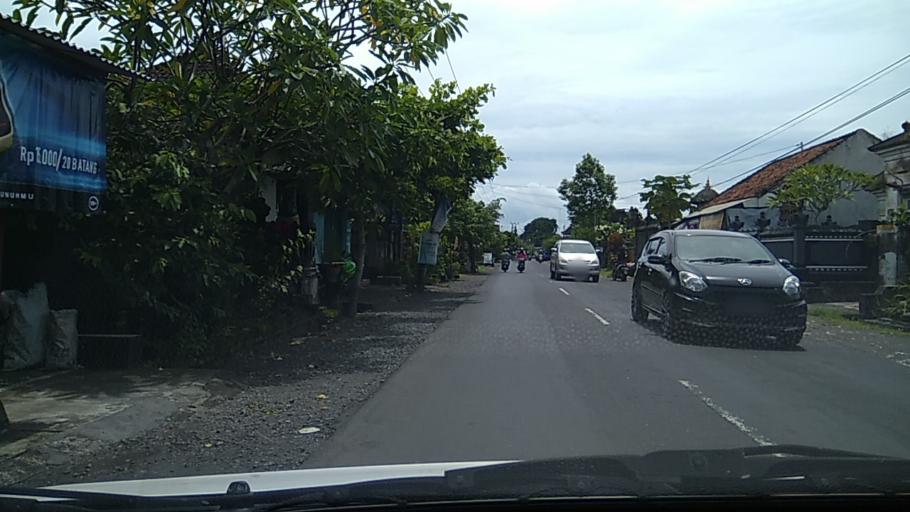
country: ID
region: Bali
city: Banjar Delodsema
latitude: -8.5887
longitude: 115.1229
